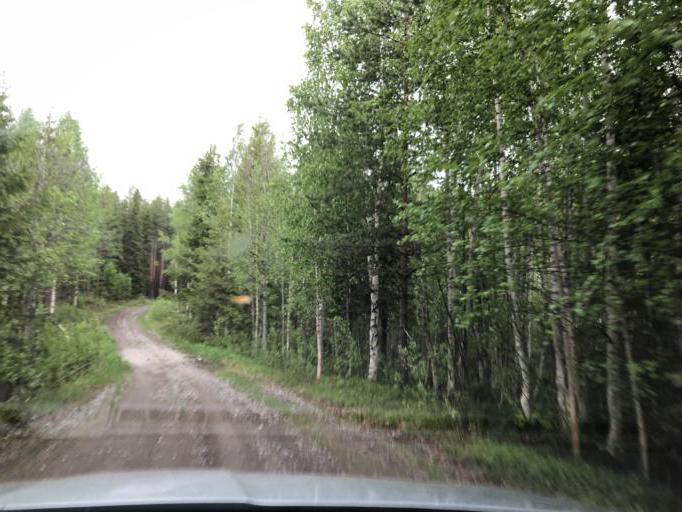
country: SE
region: Norrbotten
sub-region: Pitea Kommun
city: Roknas
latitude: 65.4034
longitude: 21.2607
